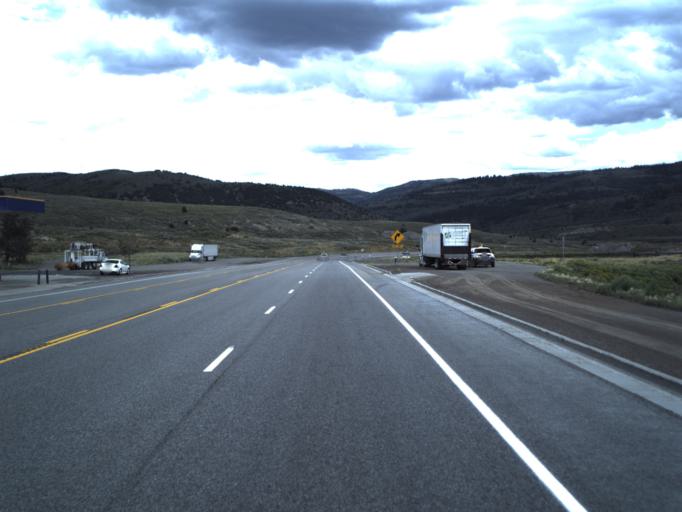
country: US
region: Utah
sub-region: Carbon County
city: Helper
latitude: 39.9284
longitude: -111.0801
